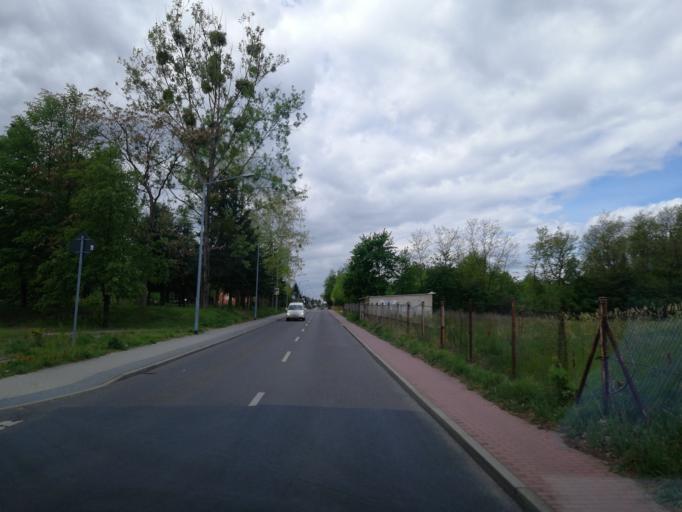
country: DE
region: Brandenburg
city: Lauchhammer
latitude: 51.5014
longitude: 13.7674
